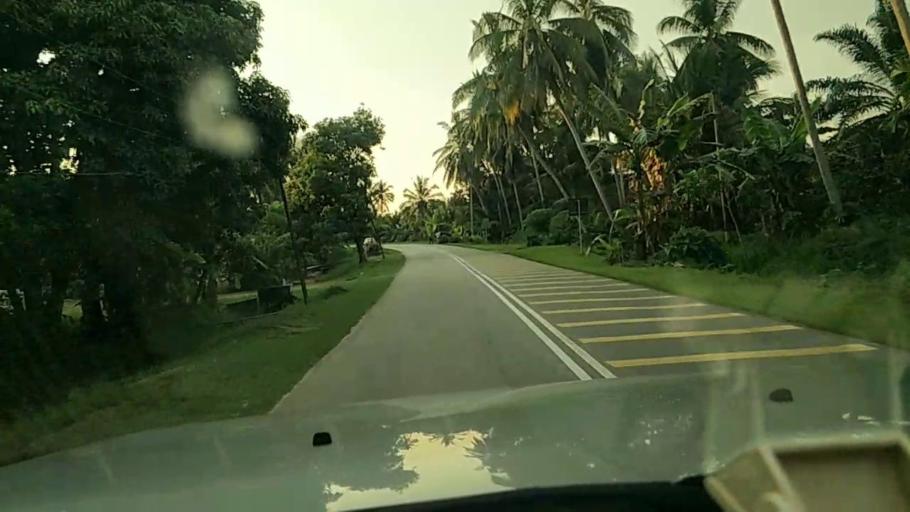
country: MY
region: Selangor
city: Kuala Selangor
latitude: 3.3044
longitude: 101.2956
